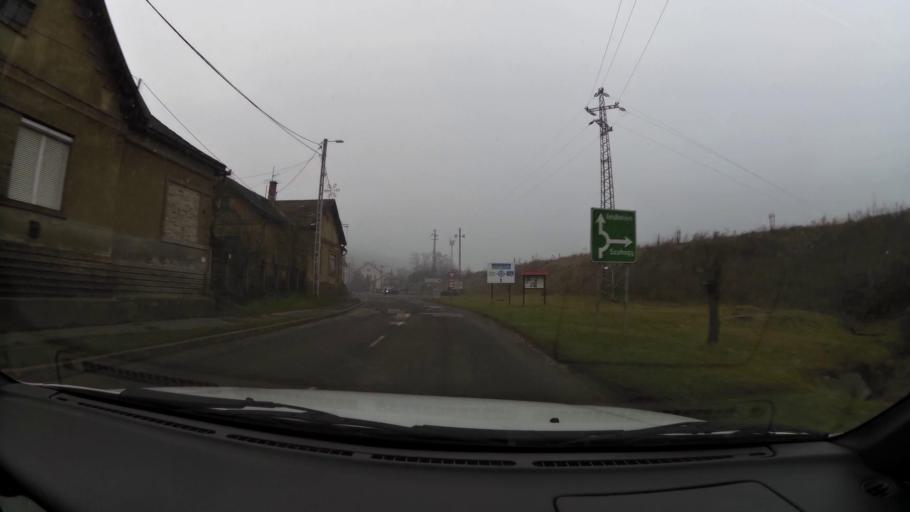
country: HU
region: Borsod-Abauj-Zemplen
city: Rudabanya
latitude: 48.3714
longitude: 20.6255
